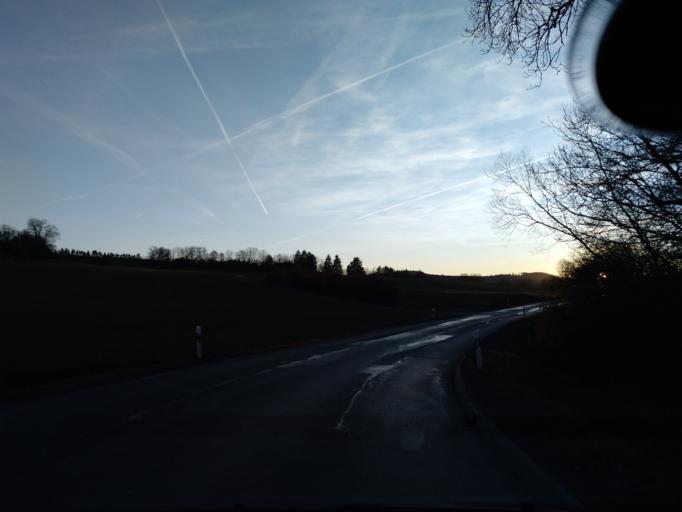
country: DE
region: Baden-Wuerttemberg
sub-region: Regierungsbezirk Stuttgart
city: Michelbach an der Bilz
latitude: 49.0565
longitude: 9.7546
